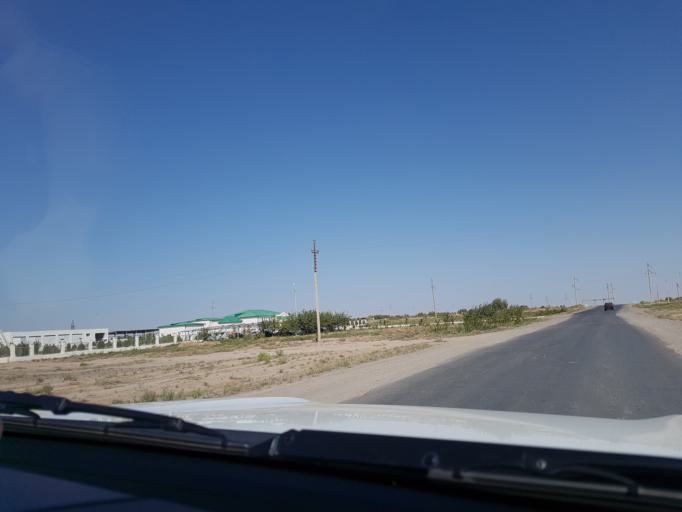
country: IR
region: Razavi Khorasan
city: Sarakhs
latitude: 36.5240
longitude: 61.2329
